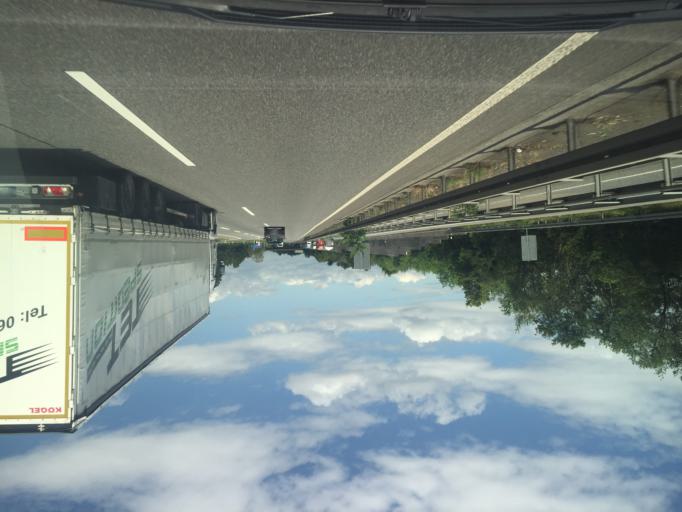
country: DE
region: Hesse
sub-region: Regierungsbezirk Darmstadt
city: Gross-Gerau
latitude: 49.9284
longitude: 8.4954
